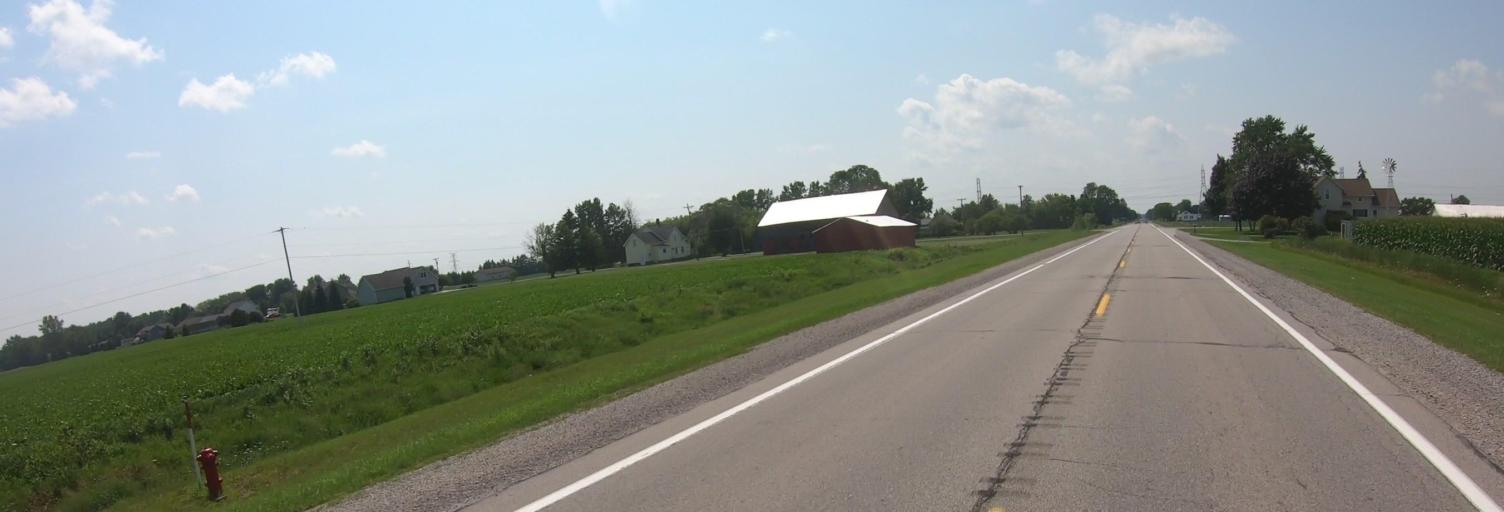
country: US
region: Michigan
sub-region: Saginaw County
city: Frankenmuth
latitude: 43.4072
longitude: -83.7756
